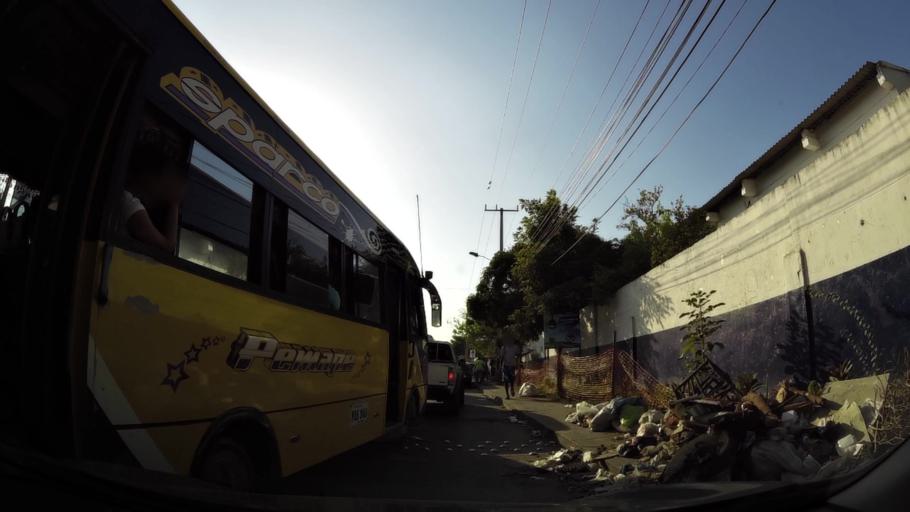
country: CO
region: Bolivar
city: Cartagena
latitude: 10.3797
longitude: -75.4819
